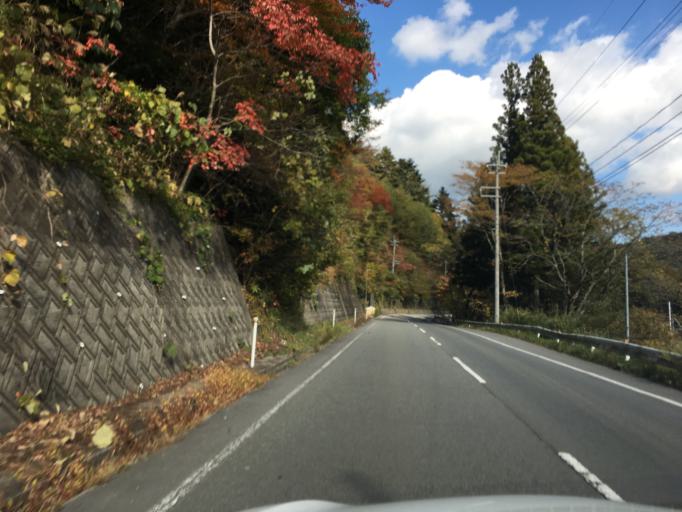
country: JP
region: Fukushima
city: Funehikimachi-funehiki
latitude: 37.3336
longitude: 140.7944
